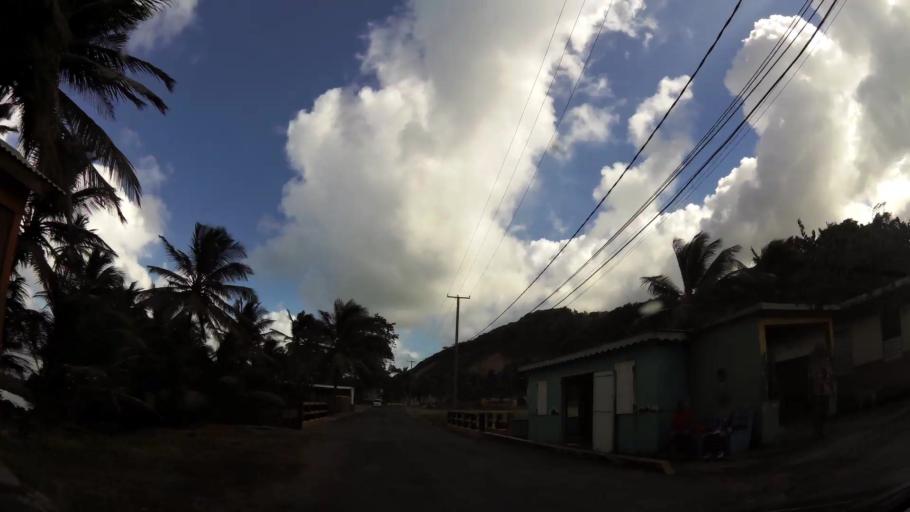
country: DM
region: Saint Andrew
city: Calibishie
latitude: 15.6006
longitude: -61.3958
